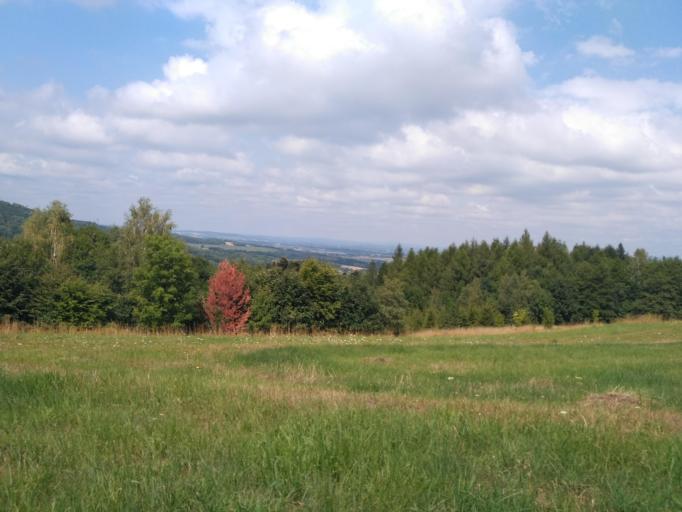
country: PL
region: Subcarpathian Voivodeship
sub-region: Powiat krosnienski
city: Iwonicz-Zdroj
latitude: 49.5759
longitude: 21.8059
